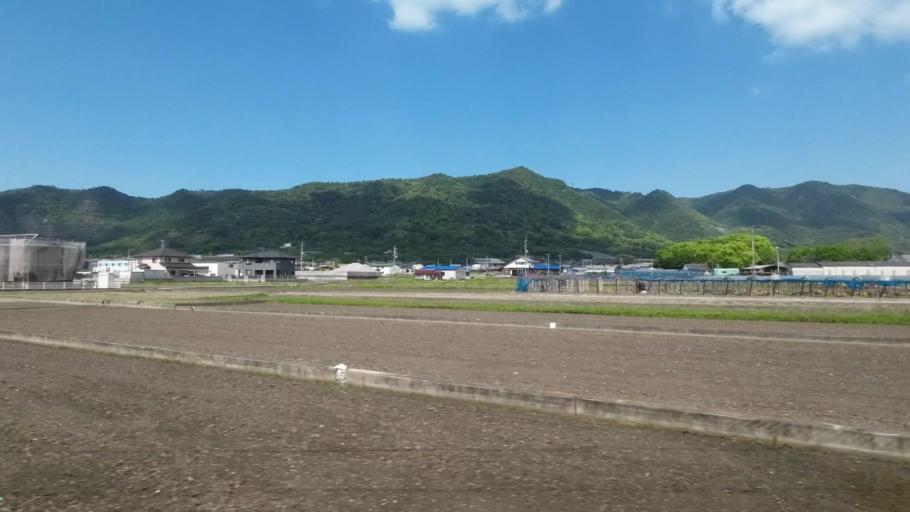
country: JP
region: Kagawa
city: Kan'onjicho
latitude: 34.1553
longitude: 133.6881
